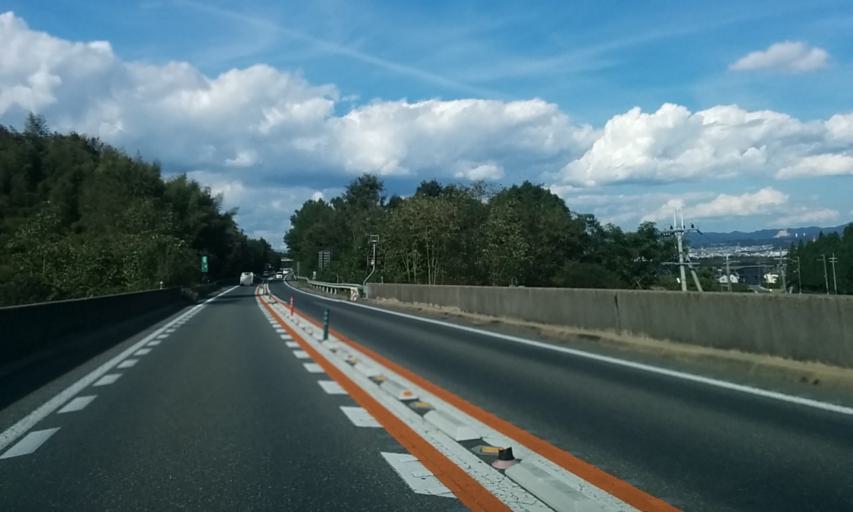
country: JP
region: Kyoto
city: Tanabe
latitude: 34.8190
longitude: 135.7513
